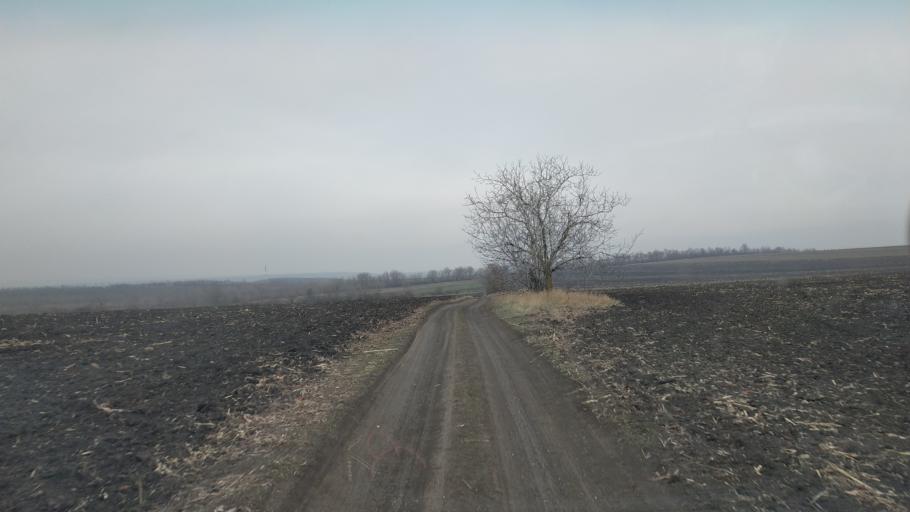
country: MD
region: Chisinau
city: Singera
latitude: 46.8283
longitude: 28.9993
